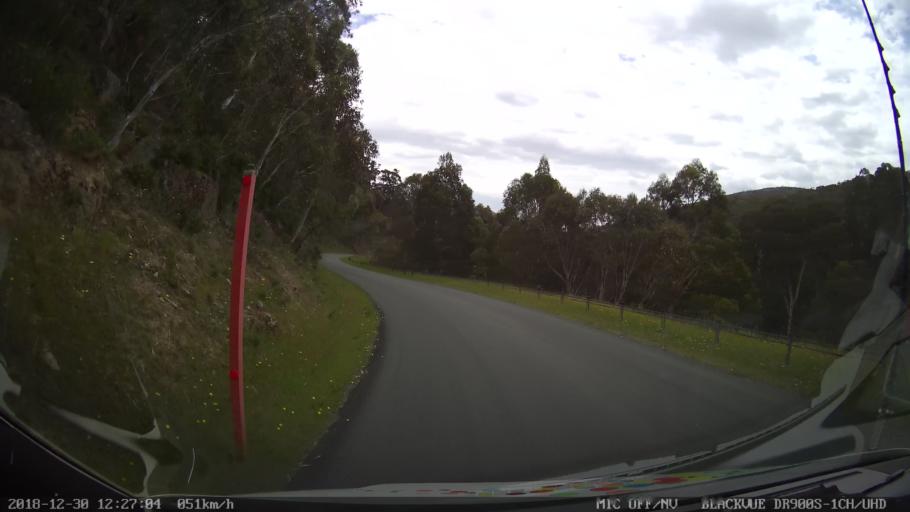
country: AU
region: New South Wales
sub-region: Snowy River
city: Jindabyne
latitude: -36.3337
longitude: 148.4903
